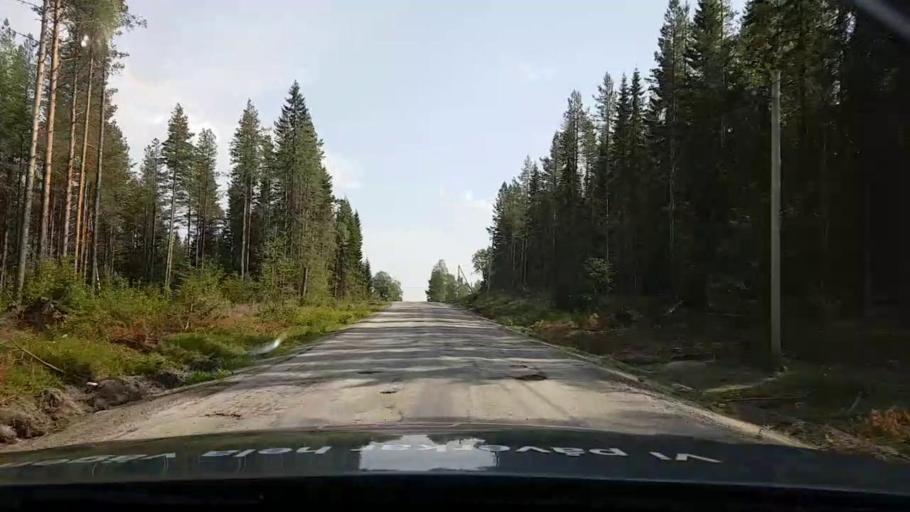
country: SE
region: Jaemtland
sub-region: Braecke Kommun
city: Braecke
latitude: 62.7319
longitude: 15.4779
